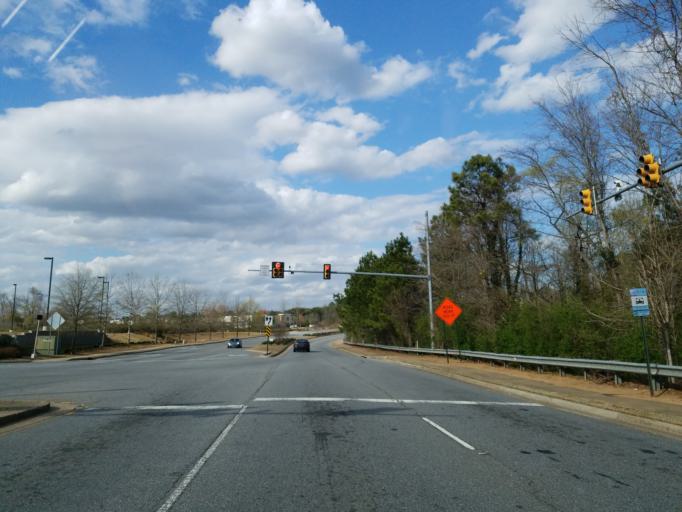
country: US
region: Georgia
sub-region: Cobb County
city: Kennesaw
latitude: 34.0191
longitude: -84.5537
